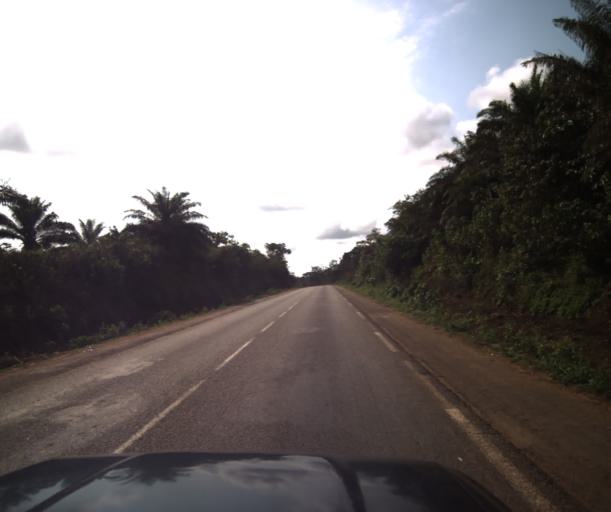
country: CM
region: Littoral
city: Edea
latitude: 3.9410
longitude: 10.0472
